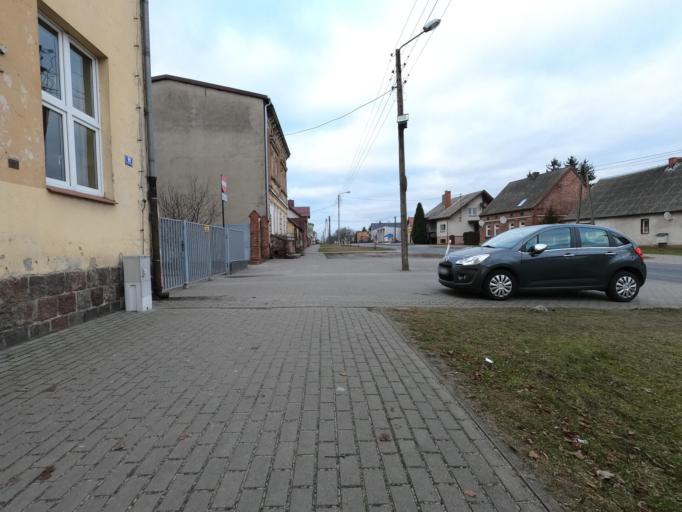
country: PL
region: Greater Poland Voivodeship
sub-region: Powiat pilski
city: Bialosliwie
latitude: 53.1052
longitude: 17.1255
